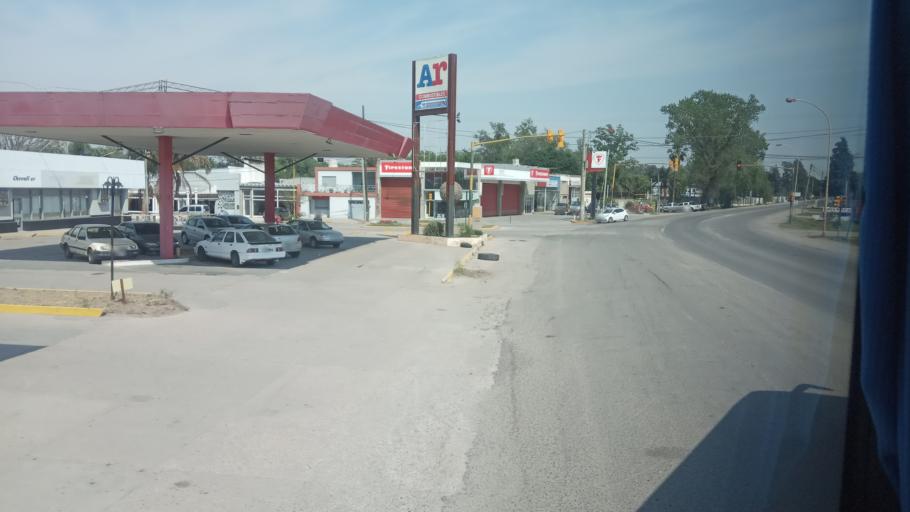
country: AR
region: Cordoba
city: Bell Ville
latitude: -32.6109
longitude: -62.6963
